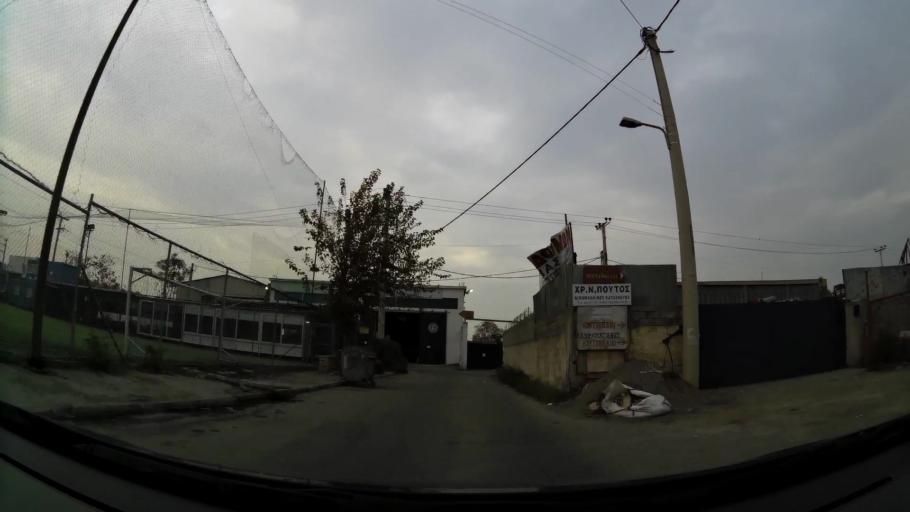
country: GR
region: Attica
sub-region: Nomos Piraios
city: Agios Ioannis Rentis
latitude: 37.9675
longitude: 23.6679
